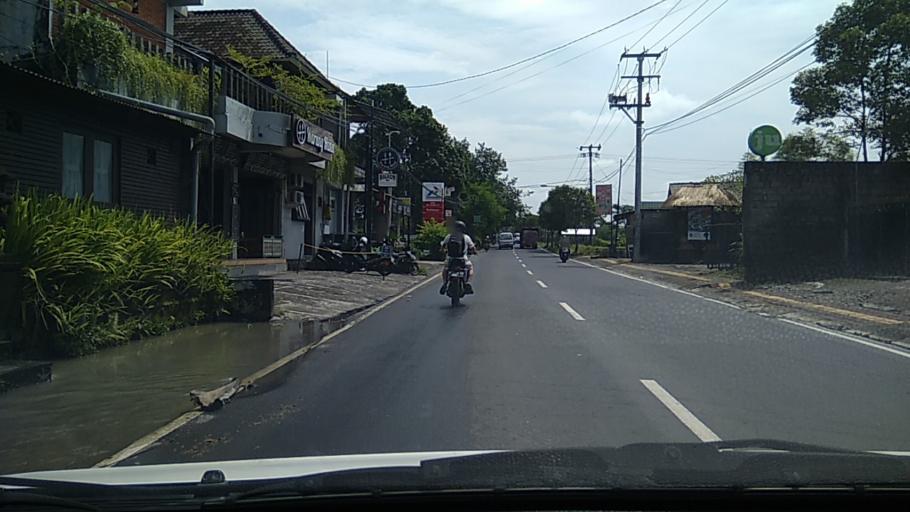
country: ID
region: Bali
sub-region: Kabupaten Gianyar
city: Ubud
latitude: -8.5234
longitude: 115.2755
